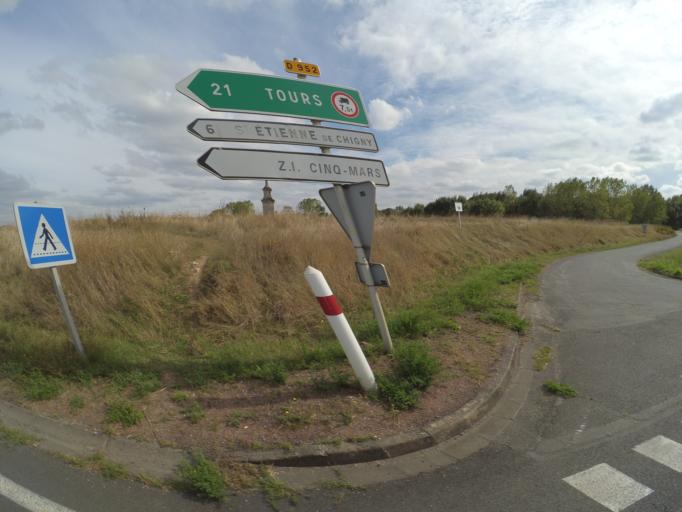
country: FR
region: Centre
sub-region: Departement d'Indre-et-Loire
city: Cinq-Mars-la-Pile
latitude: 47.3433
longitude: 0.4661
